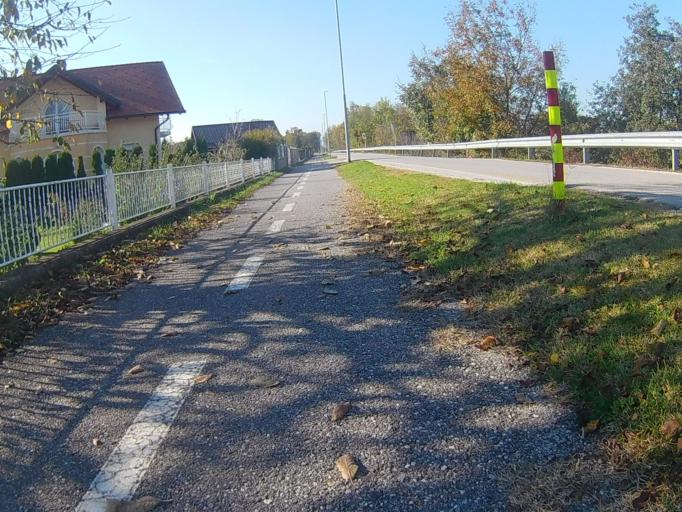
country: SI
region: Hajdina
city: Spodnja Hajdina
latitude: 46.4309
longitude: 15.8347
